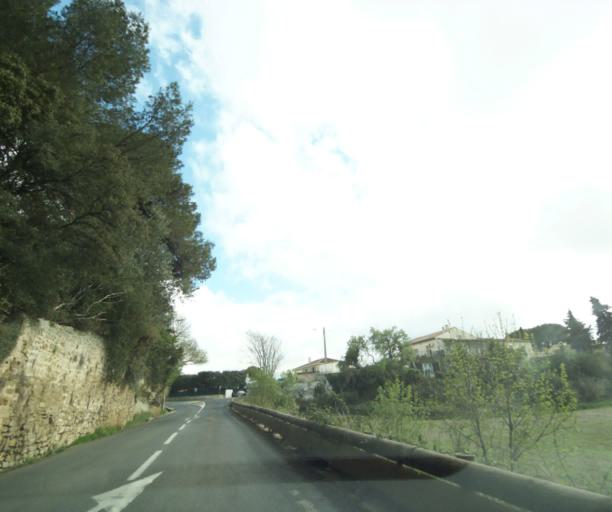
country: FR
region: Languedoc-Roussillon
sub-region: Departement de l'Herault
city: Saussan
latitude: 43.5735
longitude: 3.7719
